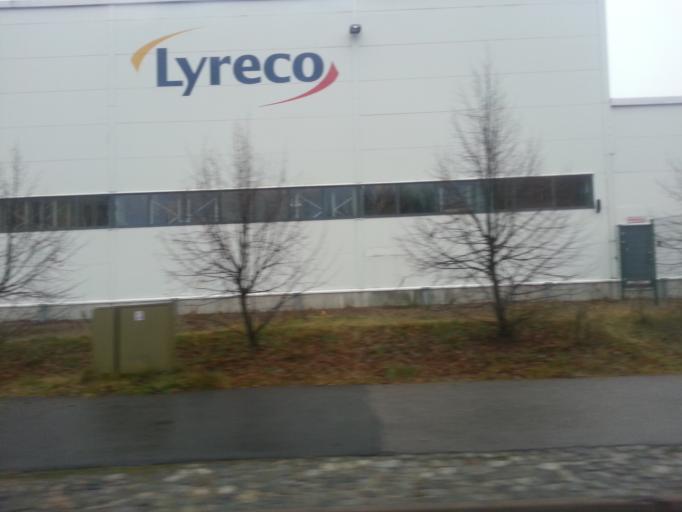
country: FI
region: Uusimaa
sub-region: Helsinki
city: Vantaa
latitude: 60.2911
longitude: 24.9525
